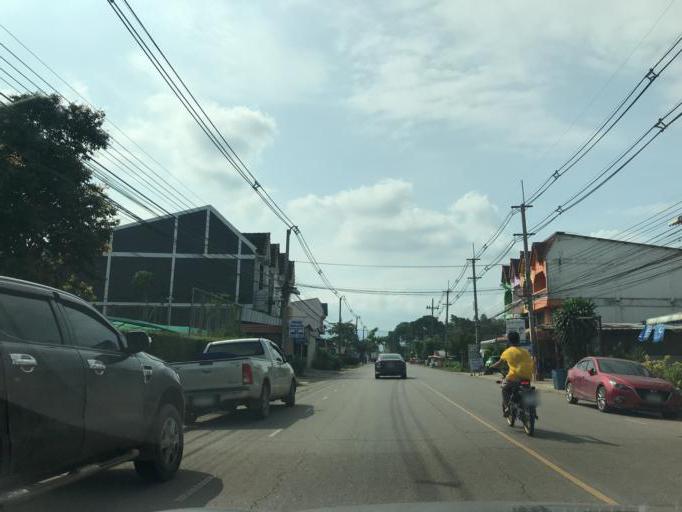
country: TH
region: Phayao
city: Chiang Kham
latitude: 19.5180
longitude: 100.3115
